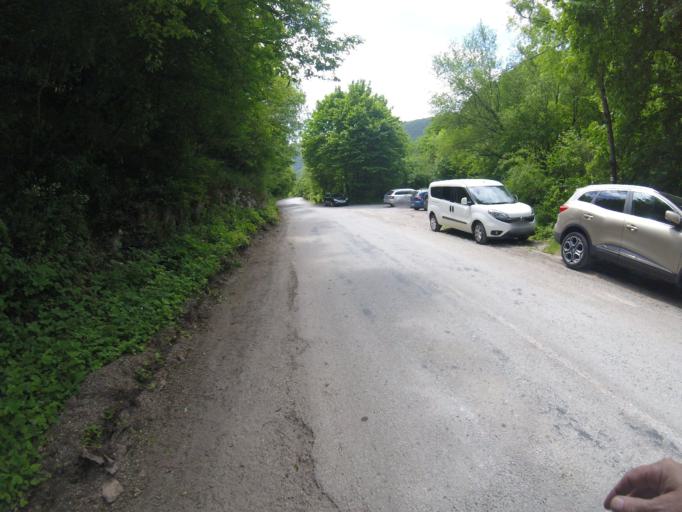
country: SK
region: Kosicky
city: Medzev
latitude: 48.6383
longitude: 20.8501
